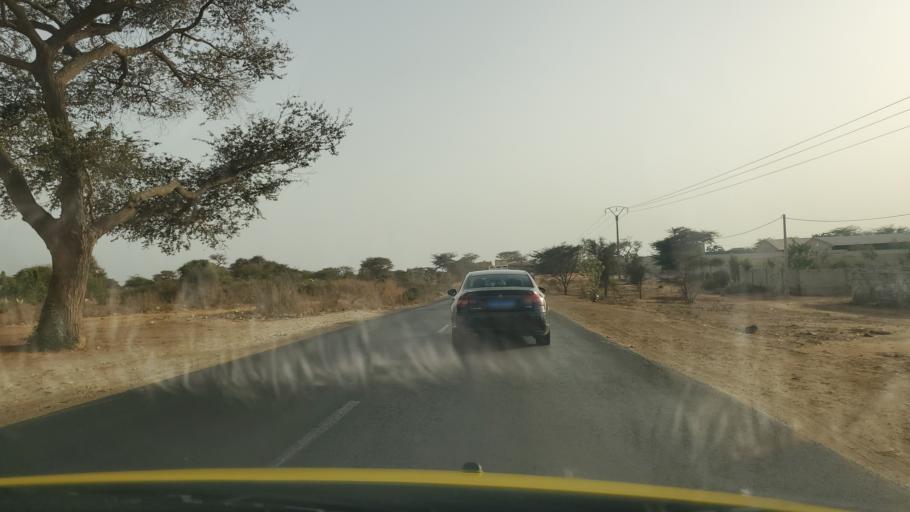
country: SN
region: Thies
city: Mekhe
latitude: 15.1006
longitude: -16.6480
